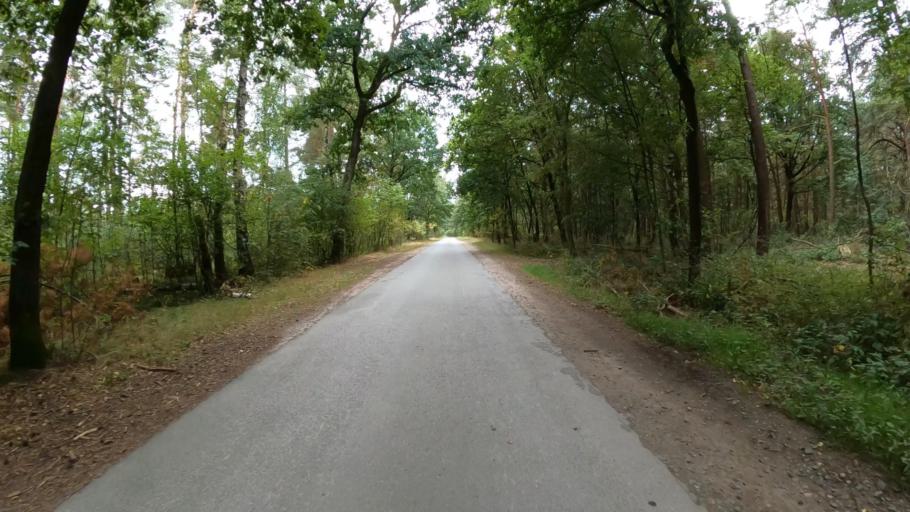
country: DE
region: Lower Saxony
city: Tostedt
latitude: 53.3068
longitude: 9.7320
